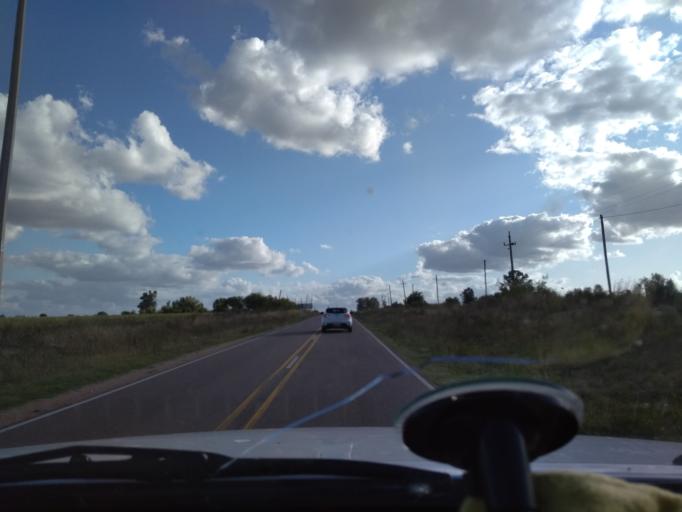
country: UY
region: Canelones
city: Tala
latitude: -34.3667
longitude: -55.7809
